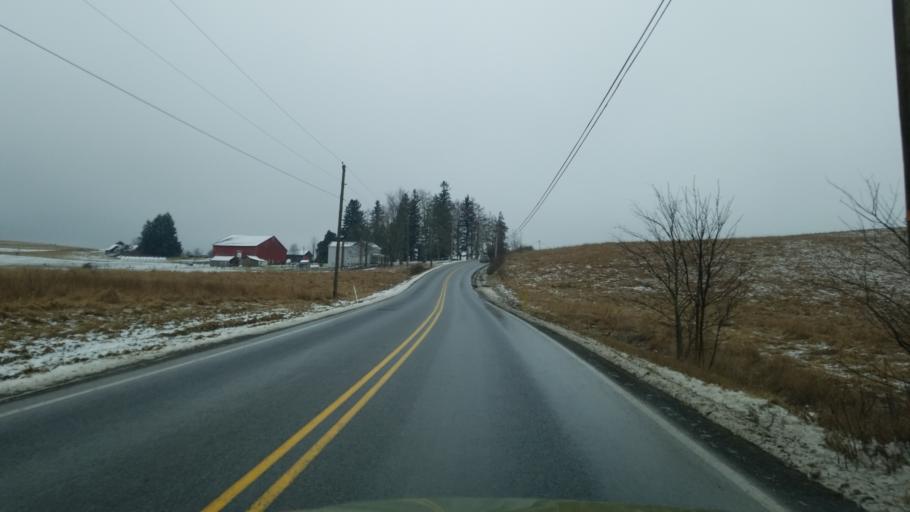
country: US
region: Pennsylvania
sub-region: Jefferson County
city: Sykesville
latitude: 41.0320
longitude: -78.7762
